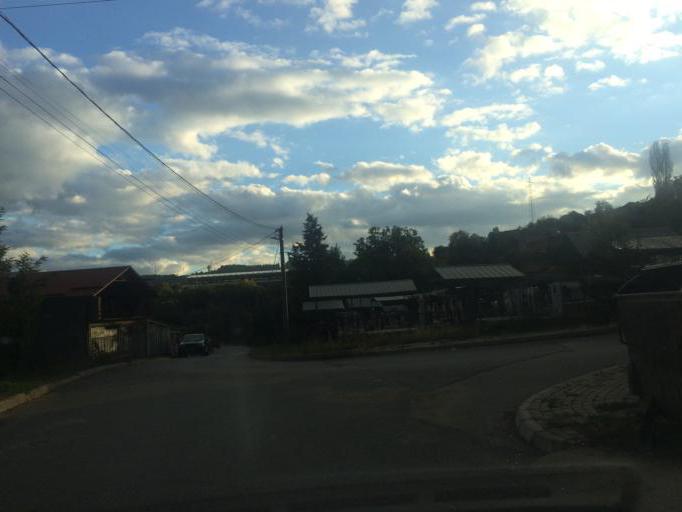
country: MK
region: Makedonska Kamenica
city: Makedonska Kamenica
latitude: 42.0248
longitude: 22.5861
